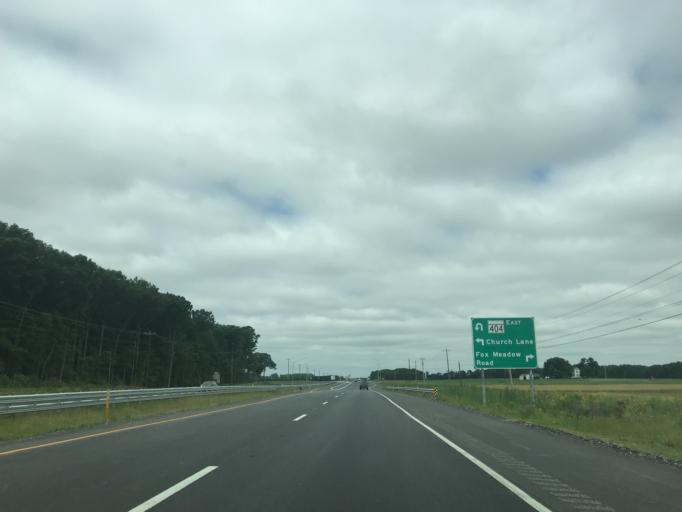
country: US
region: Maryland
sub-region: Caroline County
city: Ridgely
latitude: 38.9295
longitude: -76.0085
